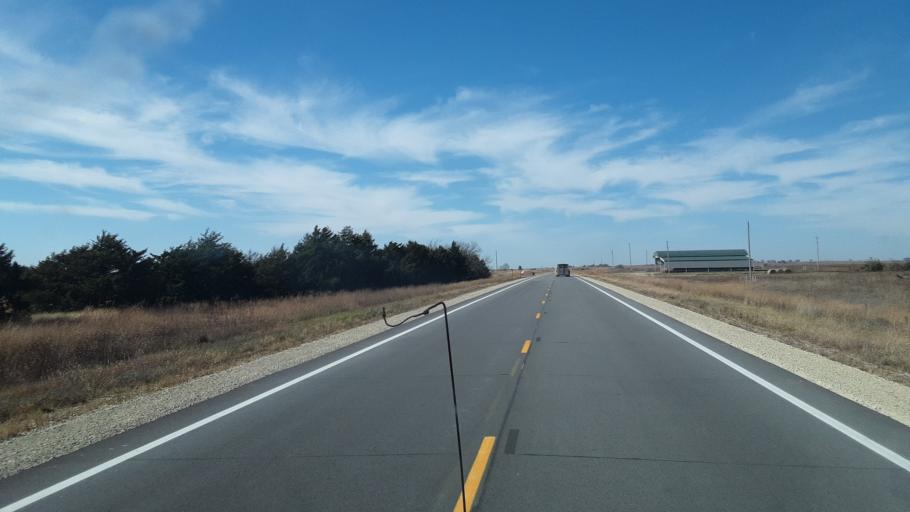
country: US
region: Kansas
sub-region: Marion County
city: Marion
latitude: 38.3629
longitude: -96.7981
